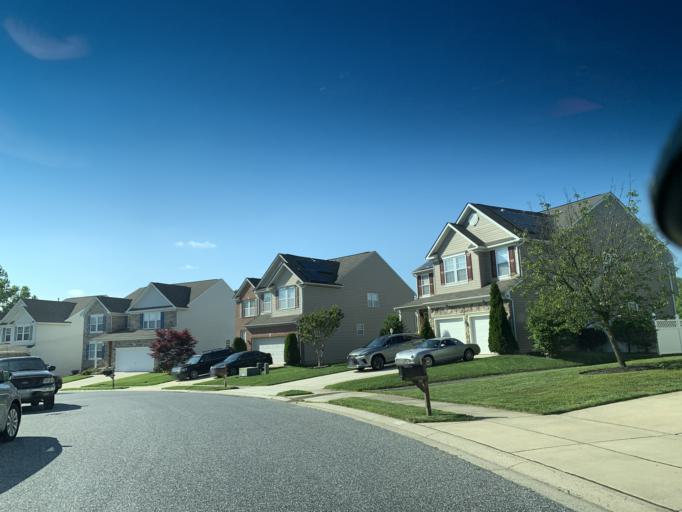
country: US
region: Maryland
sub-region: Harford County
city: Riverside
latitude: 39.4838
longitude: -76.2373
